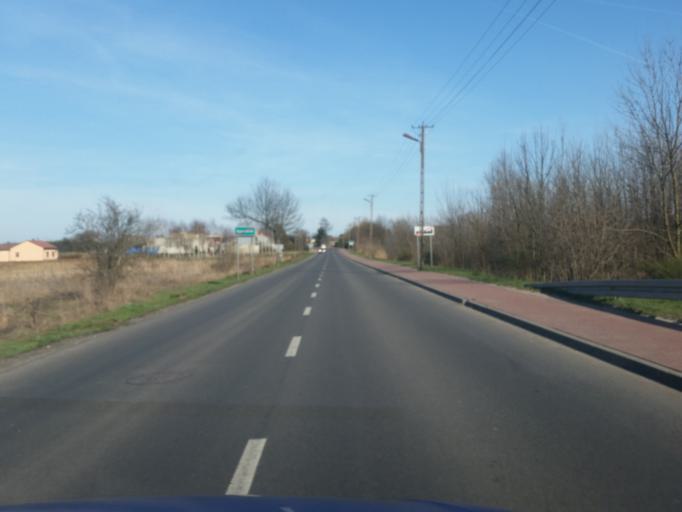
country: PL
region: Lodz Voivodeship
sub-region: Powiat radomszczanski
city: Kamiensk
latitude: 51.2031
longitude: 19.5072
